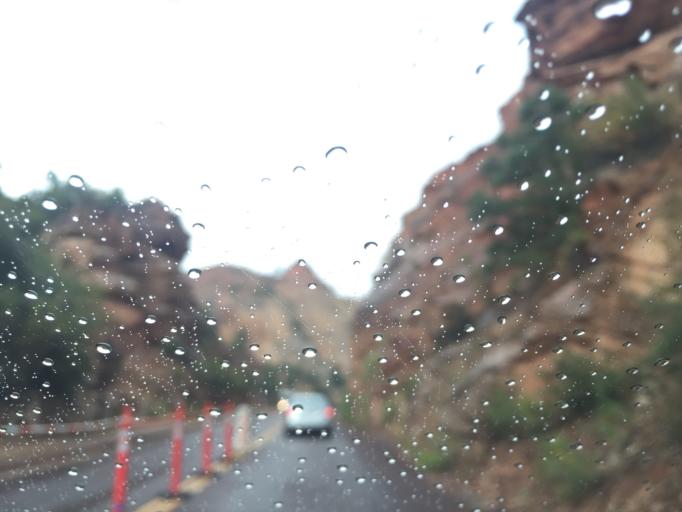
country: US
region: Utah
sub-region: Washington County
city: Hildale
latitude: 37.2136
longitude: -112.9405
